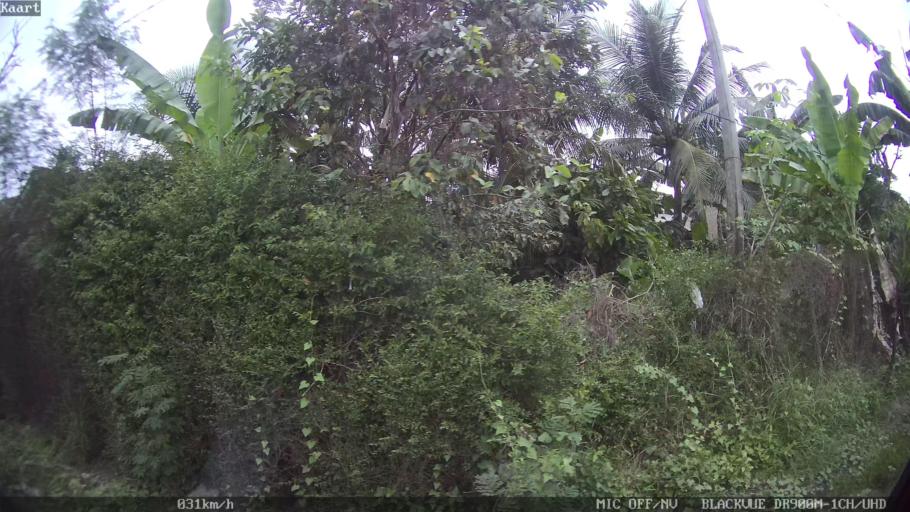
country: ID
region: Lampung
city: Gadingrejo
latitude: -5.3852
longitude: 105.0425
